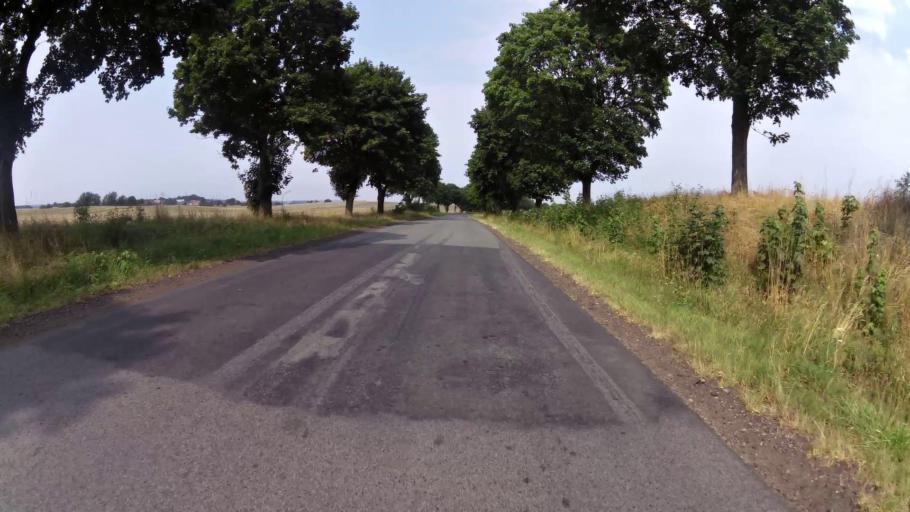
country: PL
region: West Pomeranian Voivodeship
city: Trzcinsko Zdroj
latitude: 52.9442
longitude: 14.6410
